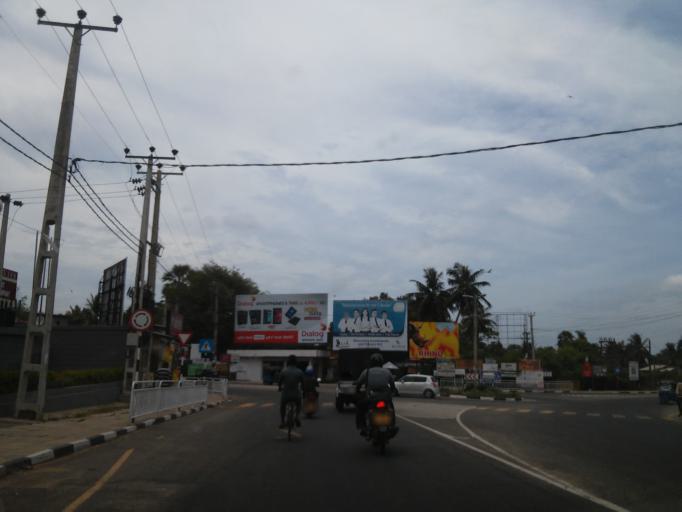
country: LK
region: Eastern Province
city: Trincomalee
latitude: 8.5873
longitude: 81.2147
